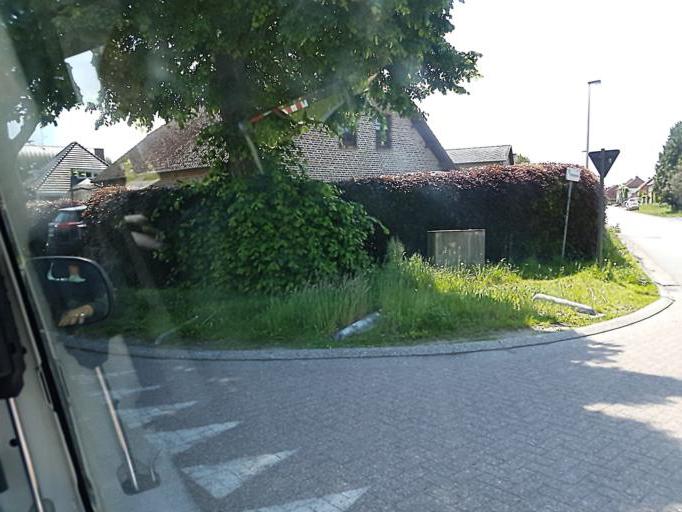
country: BE
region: Flanders
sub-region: Provincie Limburg
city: Lommel
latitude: 51.2347
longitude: 5.3152
